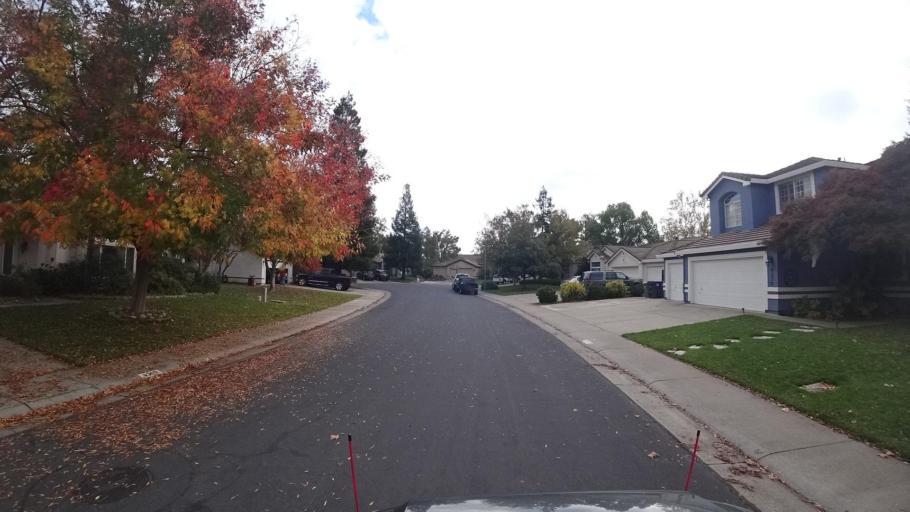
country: US
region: California
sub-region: Sacramento County
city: Elk Grove
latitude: 38.4173
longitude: -121.3617
